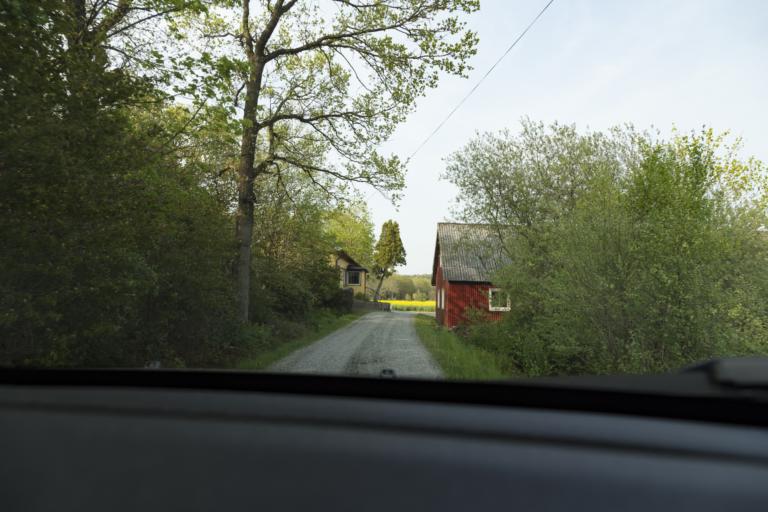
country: SE
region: Halland
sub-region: Varbergs Kommun
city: Varberg
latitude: 57.1580
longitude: 12.2484
